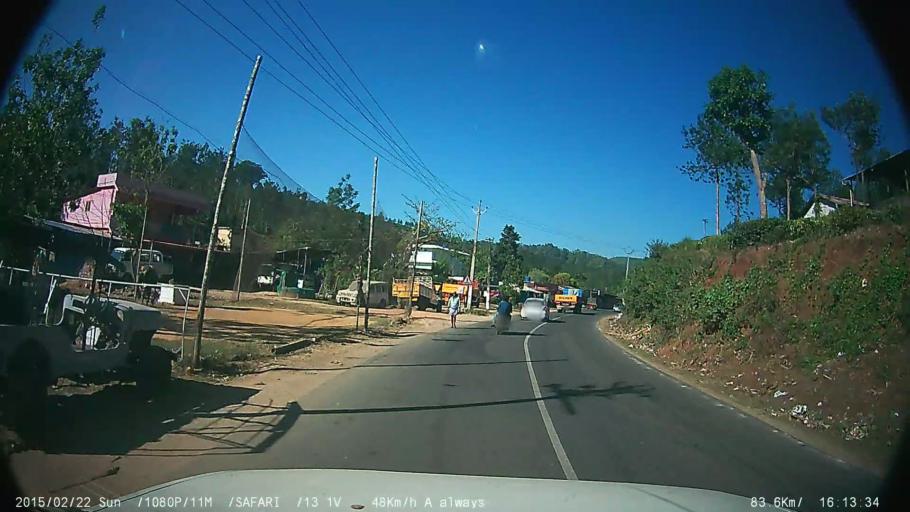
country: IN
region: Tamil Nadu
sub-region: Theni
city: Gudalur
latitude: 9.5788
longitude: 77.0975
